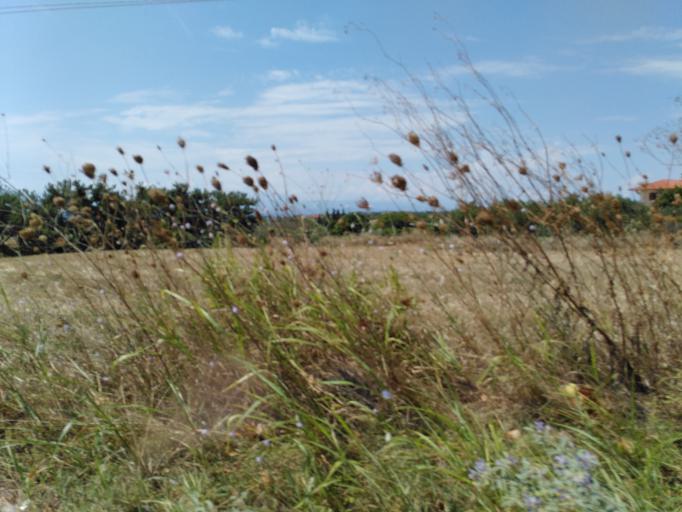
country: GR
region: Central Macedonia
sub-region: Nomos Thessalonikis
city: Nea Michaniona
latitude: 40.4795
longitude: 22.8703
